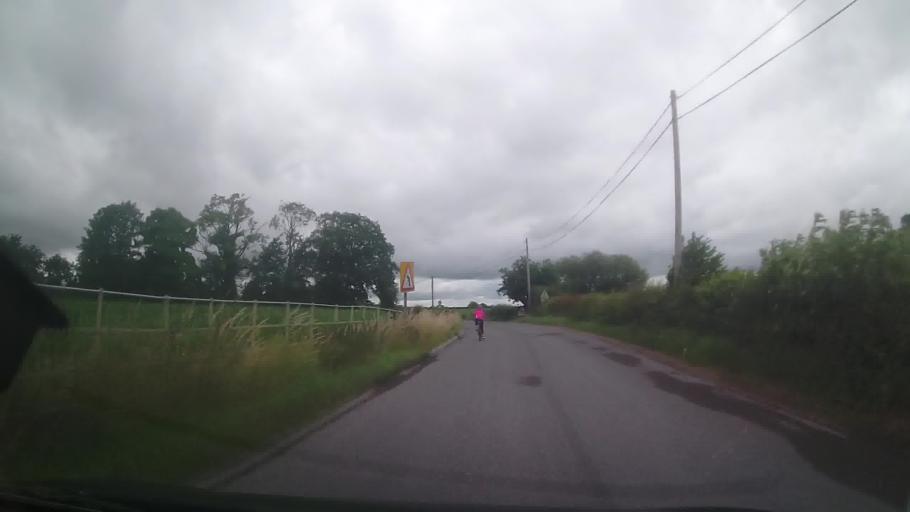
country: GB
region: England
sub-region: Shropshire
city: Petton
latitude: 52.8378
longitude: -2.8169
